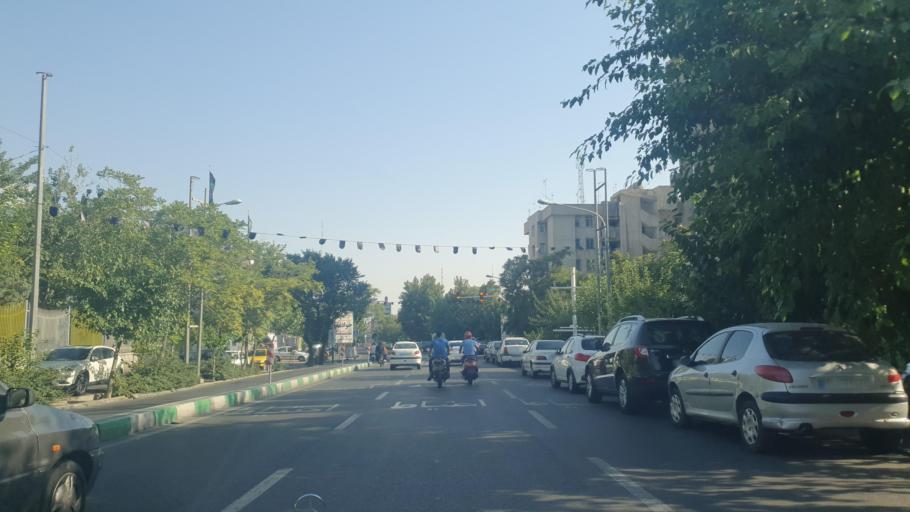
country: IR
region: Tehran
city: Tehran
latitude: 35.7118
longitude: 51.4255
